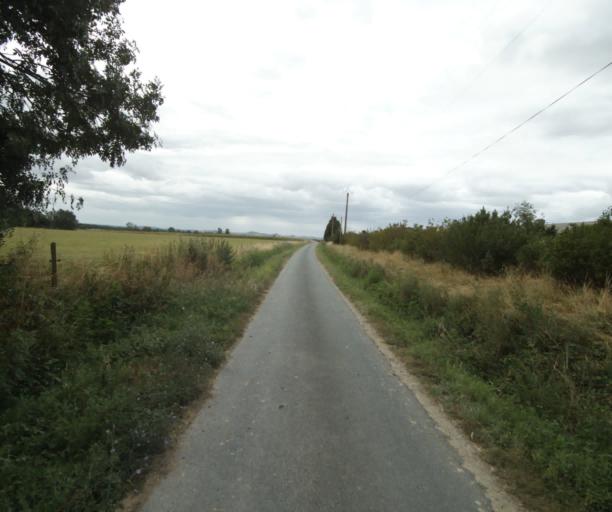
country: FR
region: Midi-Pyrenees
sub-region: Departement du Tarn
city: Soreze
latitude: 43.4700
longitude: 2.0583
